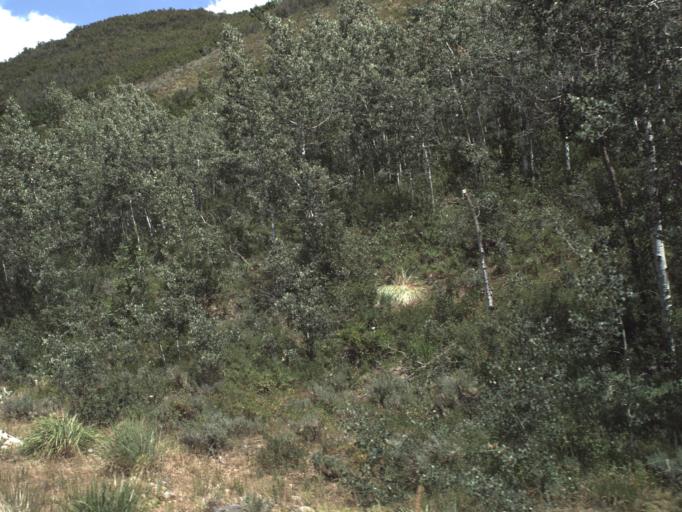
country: US
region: Utah
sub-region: Weber County
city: Wolf Creek
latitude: 41.3640
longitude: -111.5918
